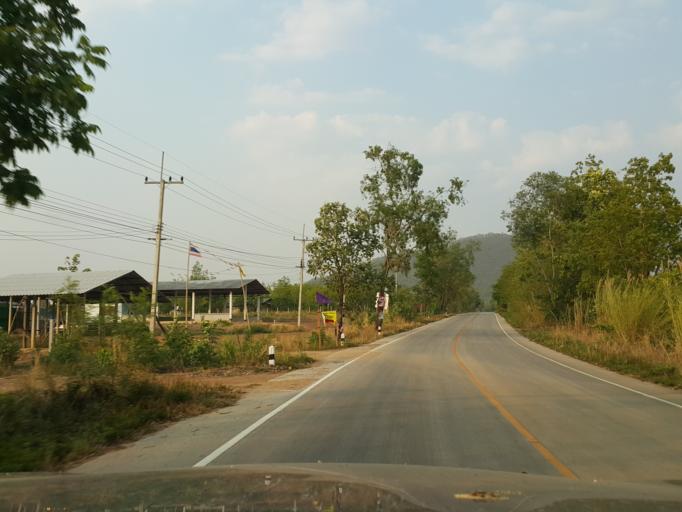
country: TH
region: Lamphun
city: Li
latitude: 17.8272
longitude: 98.9814
